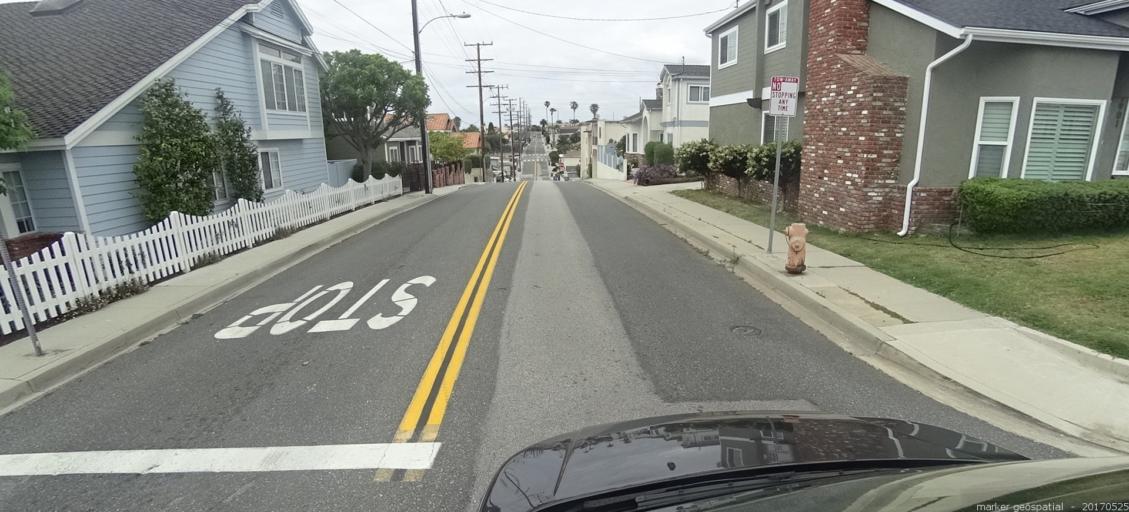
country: US
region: California
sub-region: Los Angeles County
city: Redondo Beach
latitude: 33.8671
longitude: -118.3791
